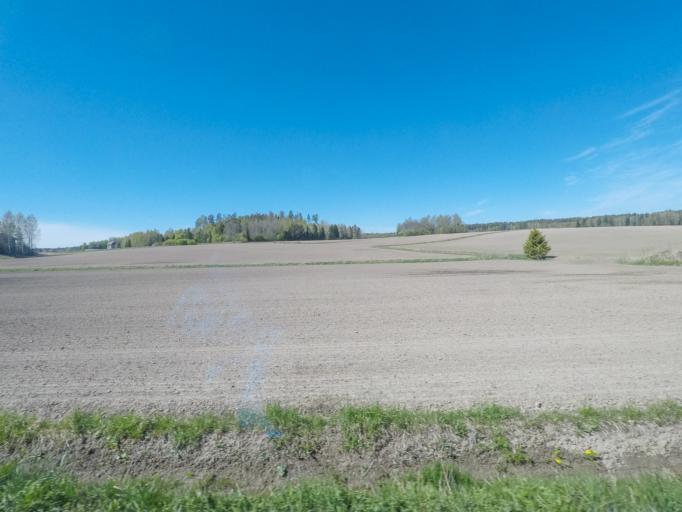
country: FI
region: Uusimaa
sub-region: Helsinki
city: Sammatti
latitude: 60.4776
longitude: 23.8277
